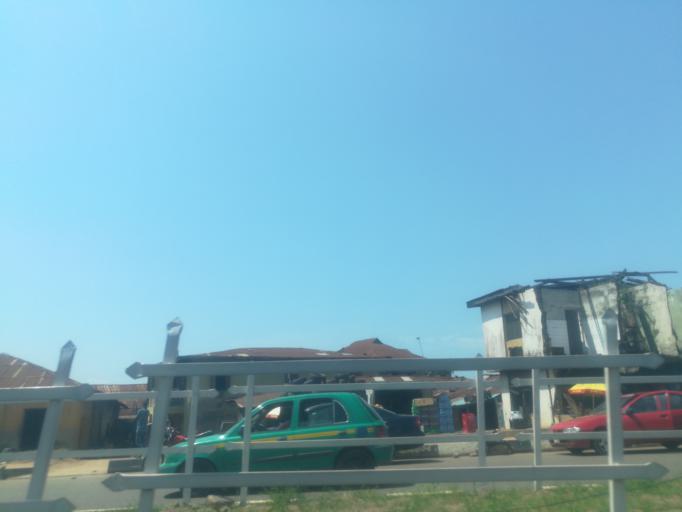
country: NG
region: Ogun
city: Abeokuta
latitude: 7.1640
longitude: 3.3513
